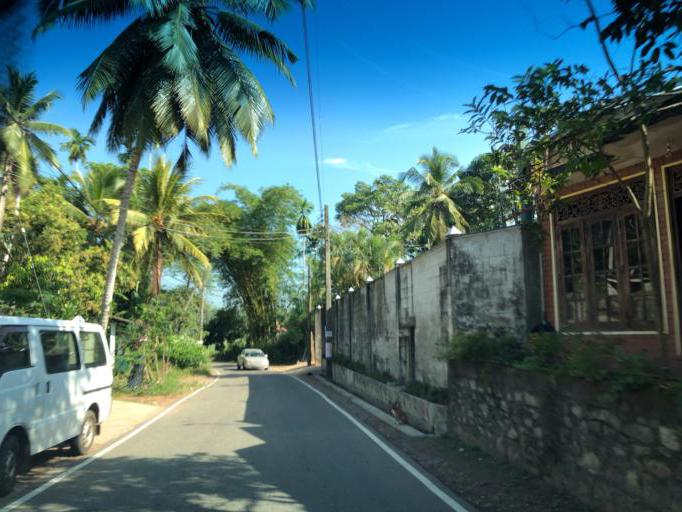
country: LK
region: Western
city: Homagama
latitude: 6.7977
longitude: 79.9819
